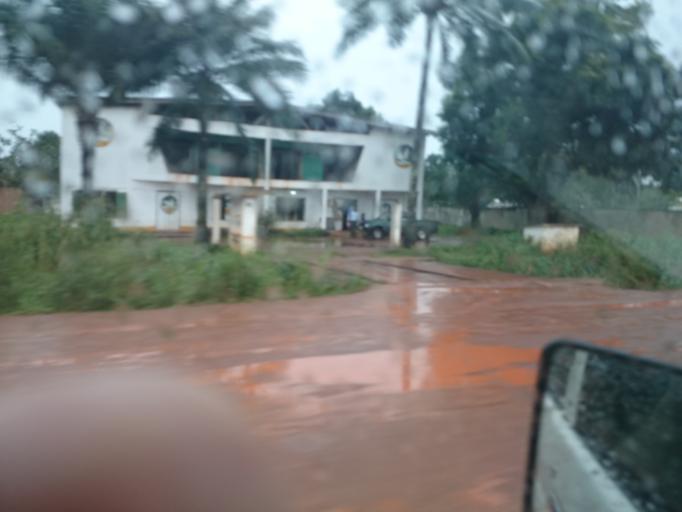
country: CF
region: Bangui
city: Bangui
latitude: 4.3680
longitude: 18.5620
